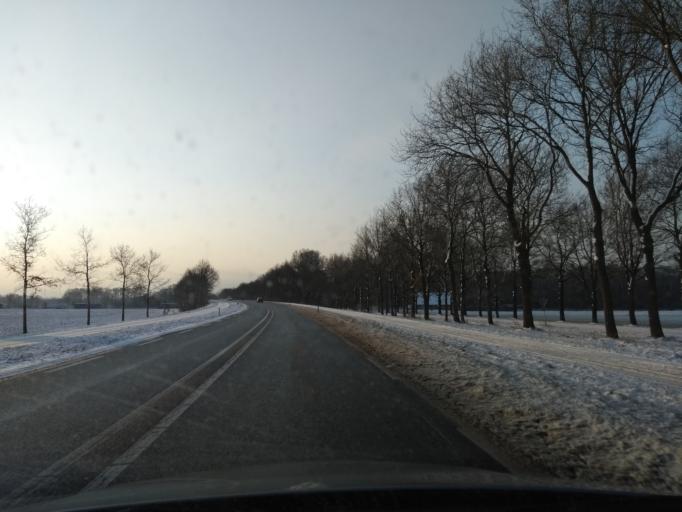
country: NL
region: Overijssel
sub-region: Gemeente Almelo
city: Almelo
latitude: 52.3001
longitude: 6.6568
